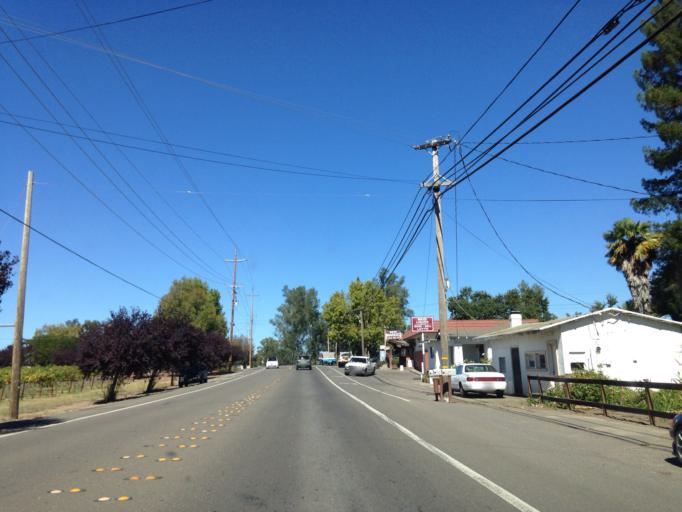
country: US
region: California
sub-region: Sonoma County
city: Windsor
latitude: 38.5763
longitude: -122.8425
